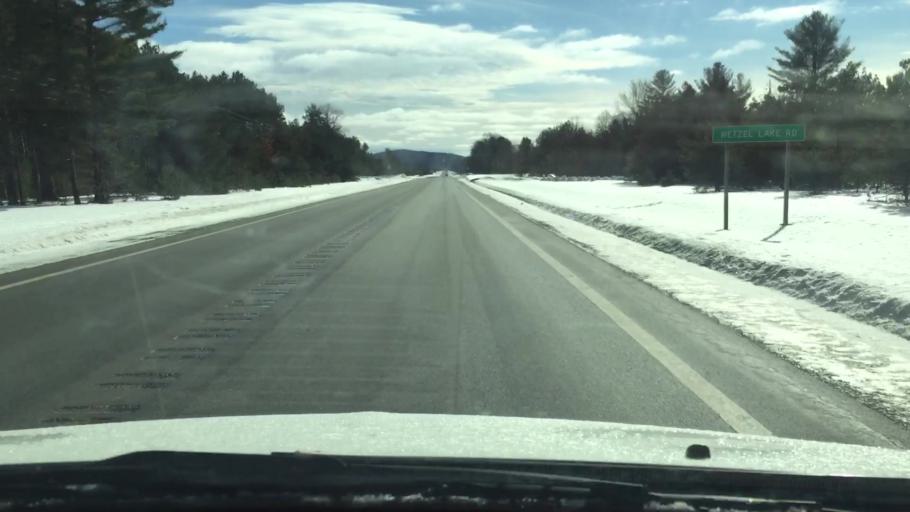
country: US
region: Michigan
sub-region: Antrim County
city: Mancelona
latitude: 44.9334
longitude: -85.0509
